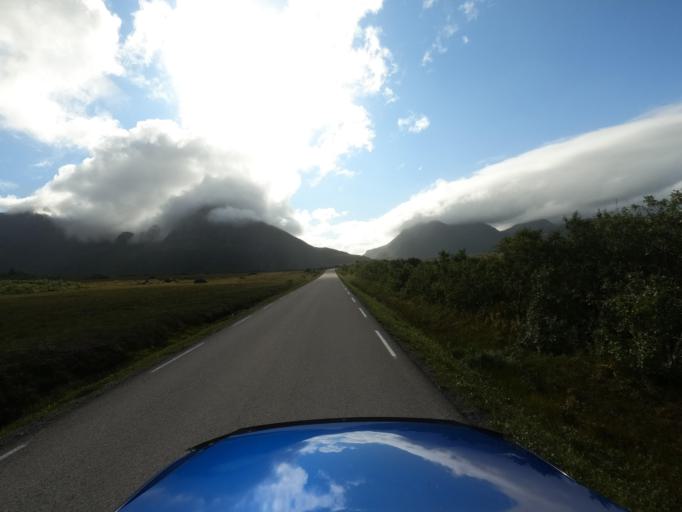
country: NO
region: Nordland
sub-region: Vagan
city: Kabelvag
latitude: 68.2957
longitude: 14.1678
